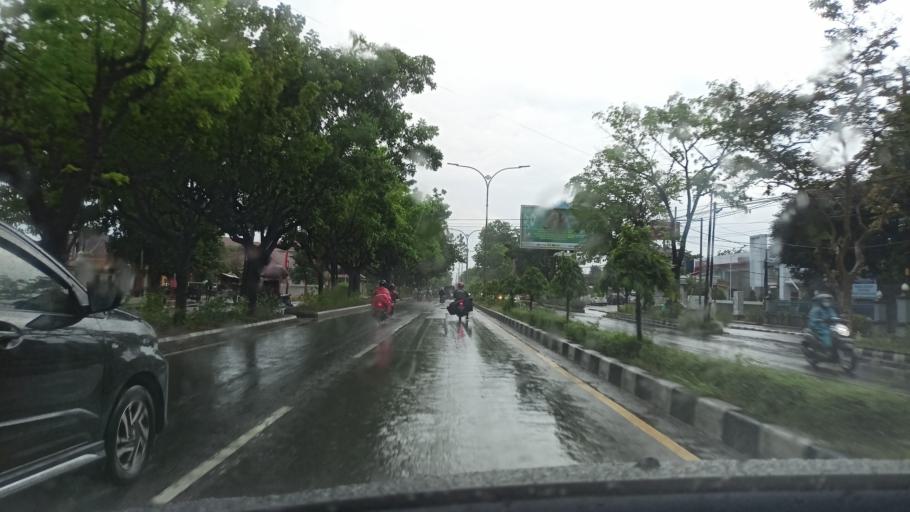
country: ID
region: Central Java
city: Colomadu
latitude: -7.5486
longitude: 110.7835
